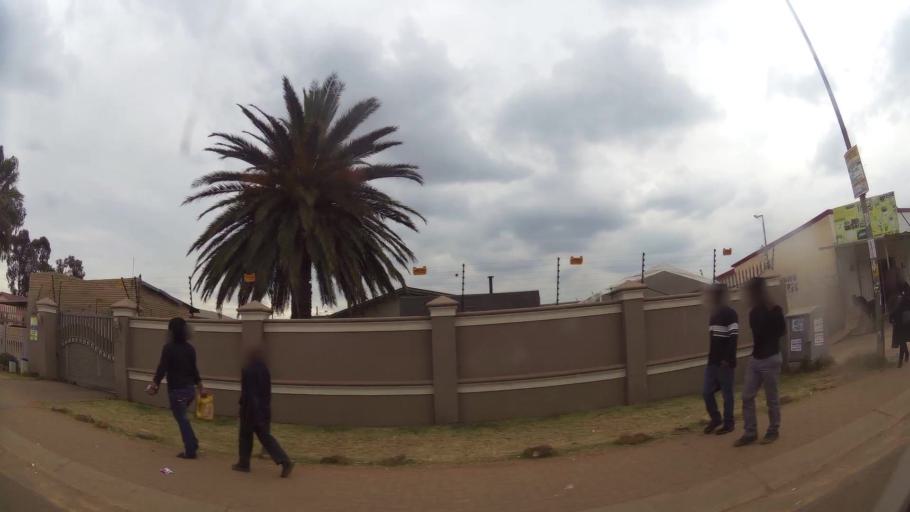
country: ZA
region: Gauteng
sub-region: Ekurhuleni Metropolitan Municipality
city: Germiston
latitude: -26.3907
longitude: 28.1417
